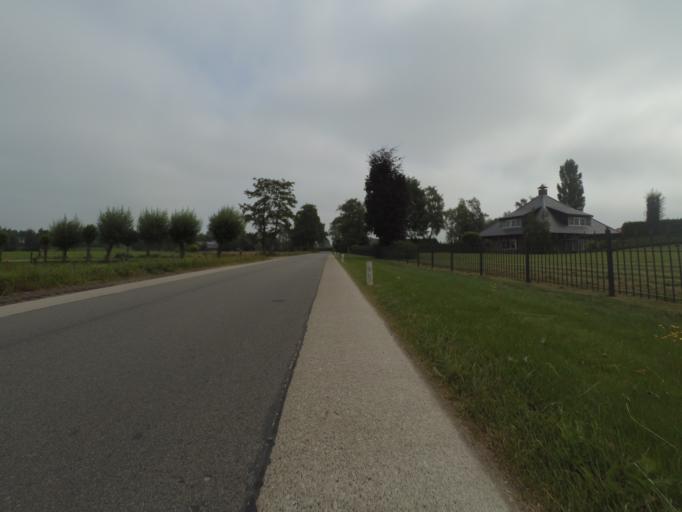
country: NL
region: Gelderland
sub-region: Gemeente Barneveld
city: Kootwijkerbroek
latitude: 52.1448
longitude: 5.6598
